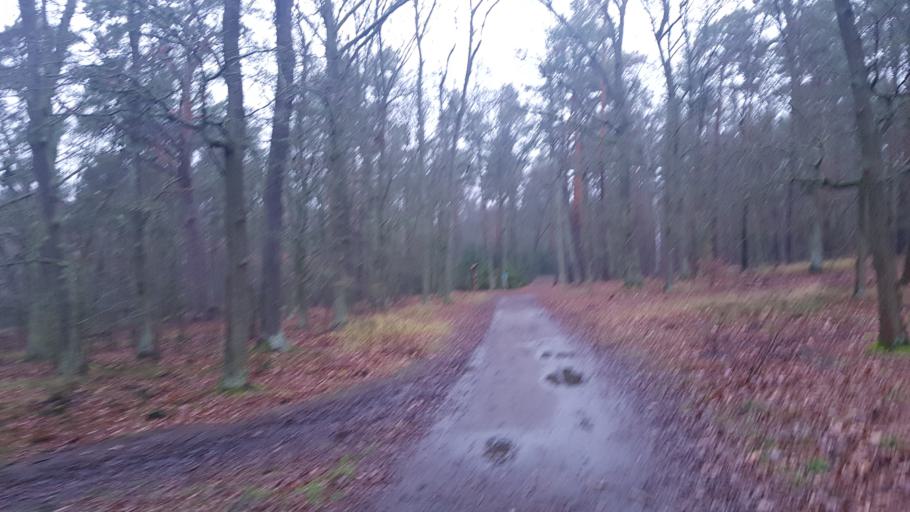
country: DE
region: Brandenburg
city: Stahnsdorf
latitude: 52.3428
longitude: 13.1526
